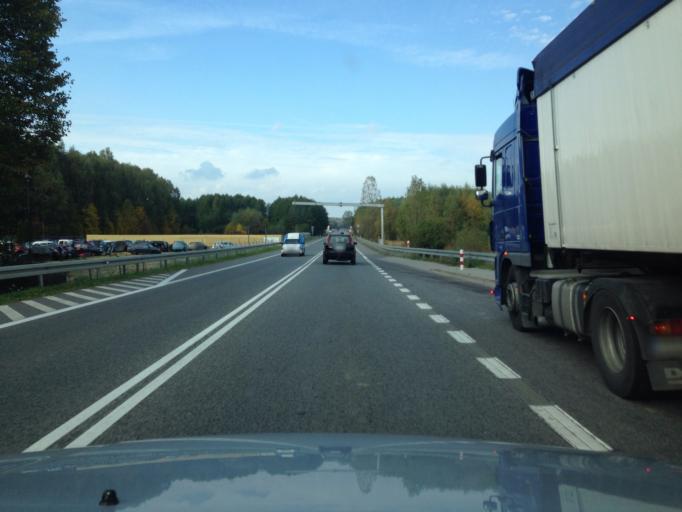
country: PL
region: Kujawsko-Pomorskie
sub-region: Powiat swiecki
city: Warlubie
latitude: 53.5278
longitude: 18.6812
